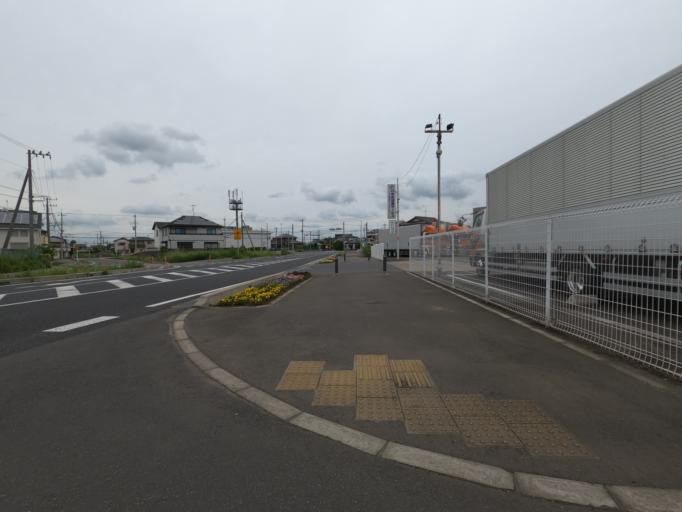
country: JP
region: Ibaraki
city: Moriya
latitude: 35.9504
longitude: 139.9822
